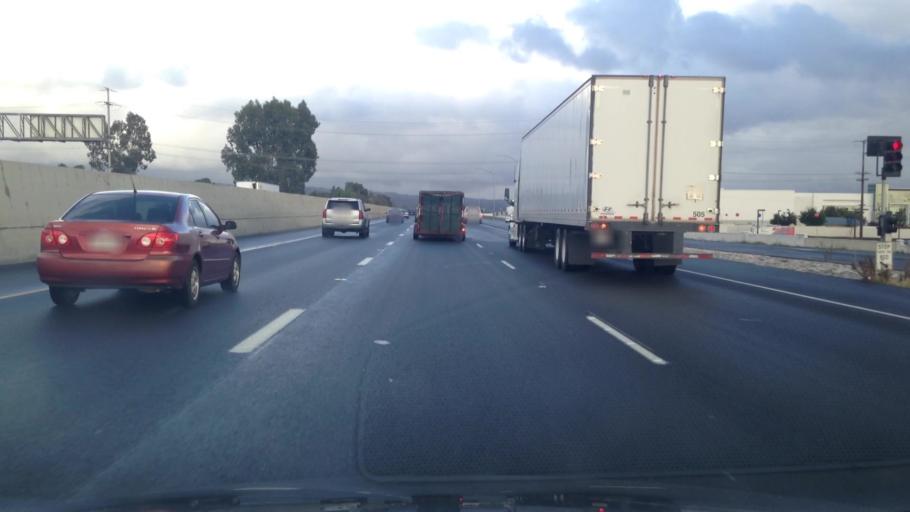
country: US
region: California
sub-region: Riverside County
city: Moreno Valley
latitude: 33.9392
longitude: -117.1762
